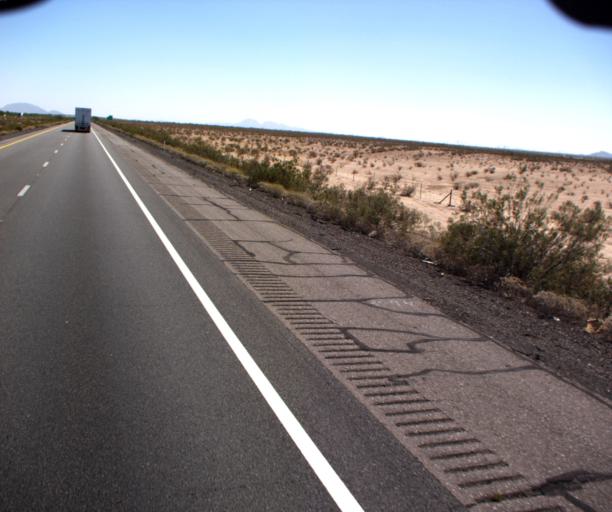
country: US
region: Arizona
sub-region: La Paz County
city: Salome
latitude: 33.5725
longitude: -113.3779
